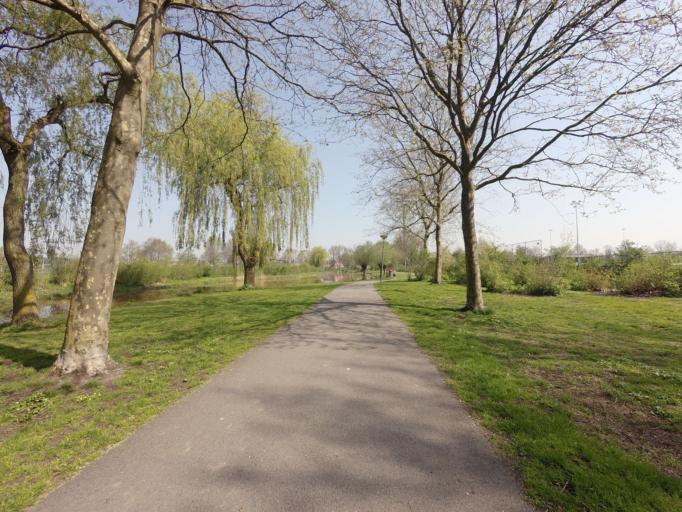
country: NL
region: Utrecht
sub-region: Gemeente De Ronde Venen
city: Mijdrecht
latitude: 52.1987
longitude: 4.8591
